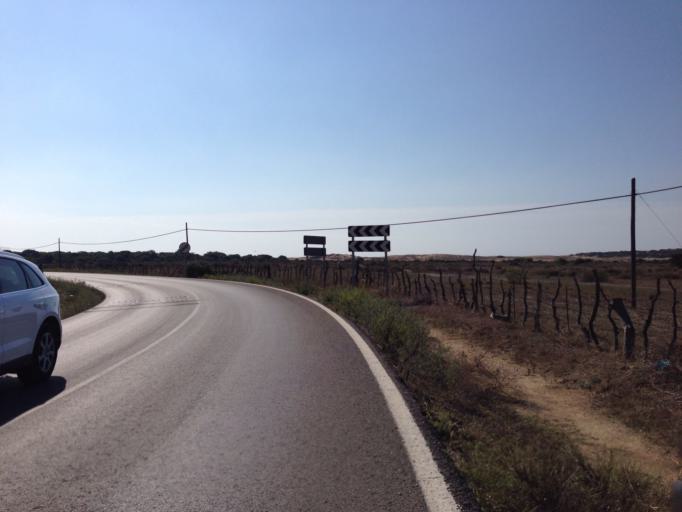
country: ES
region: Andalusia
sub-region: Provincia de Cadiz
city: Vejer de la Frontera
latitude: 36.1925
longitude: -6.0311
